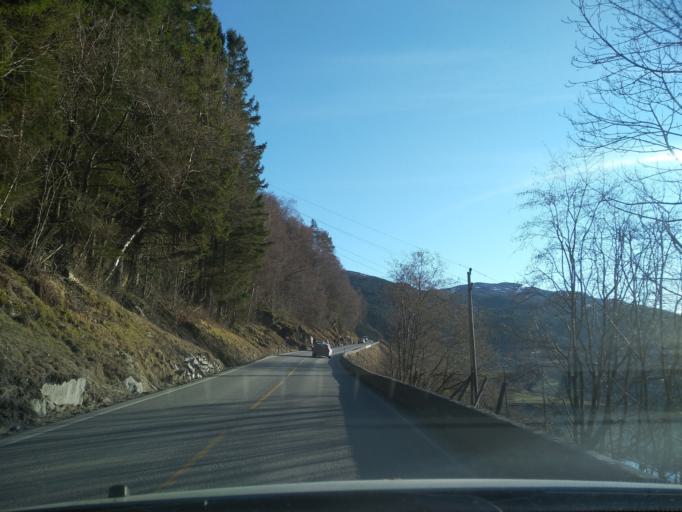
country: NO
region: Hordaland
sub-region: Etne
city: Etne
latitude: 59.6501
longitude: 5.9240
